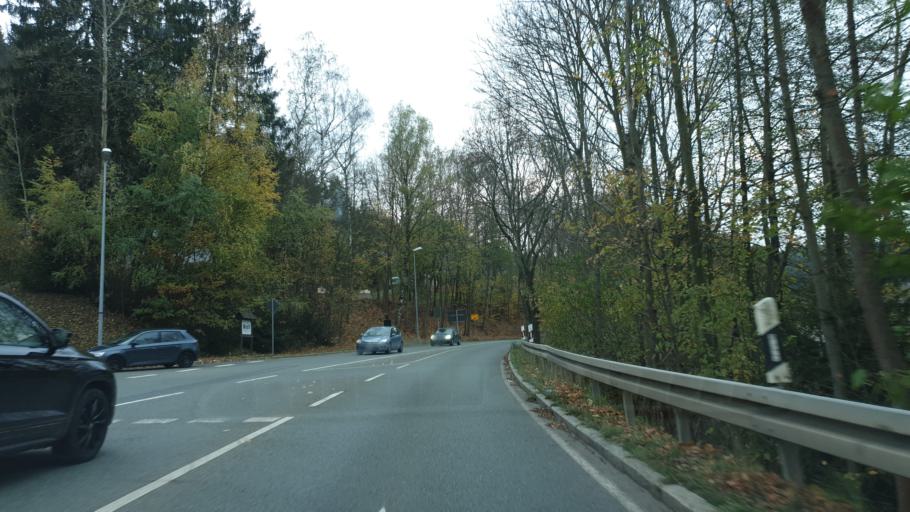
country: DE
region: Saxony
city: Schwarzenberg
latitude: 50.5173
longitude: 12.7813
